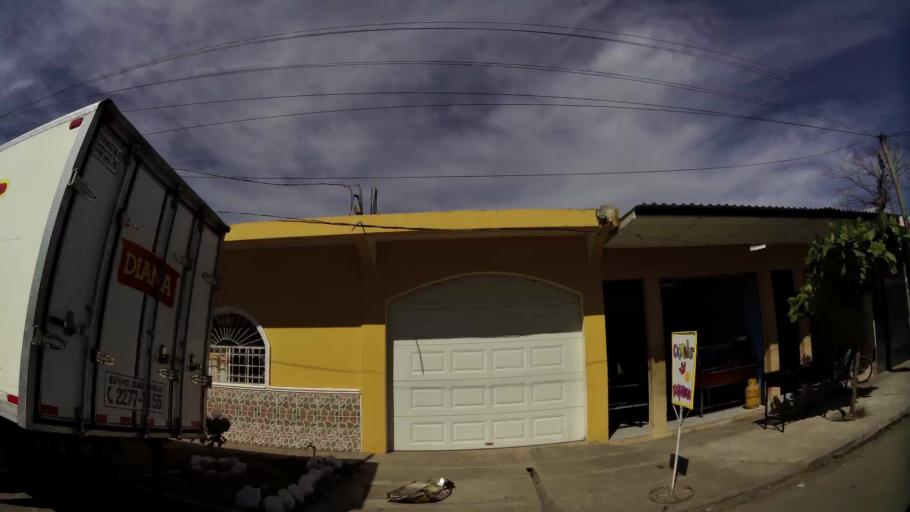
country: SV
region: San Salvador
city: Aguilares
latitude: 13.9593
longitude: -89.1866
